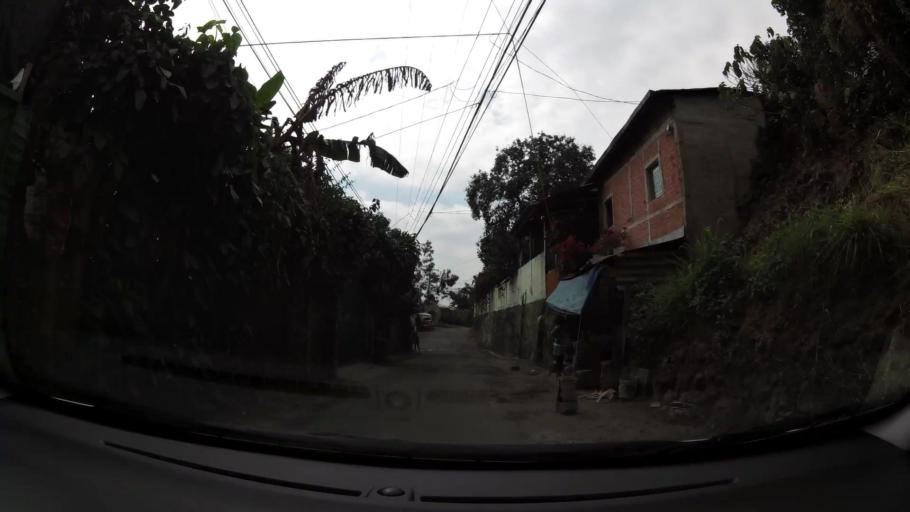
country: SV
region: La Libertad
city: Santa Tecla
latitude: 13.7088
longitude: -89.2623
